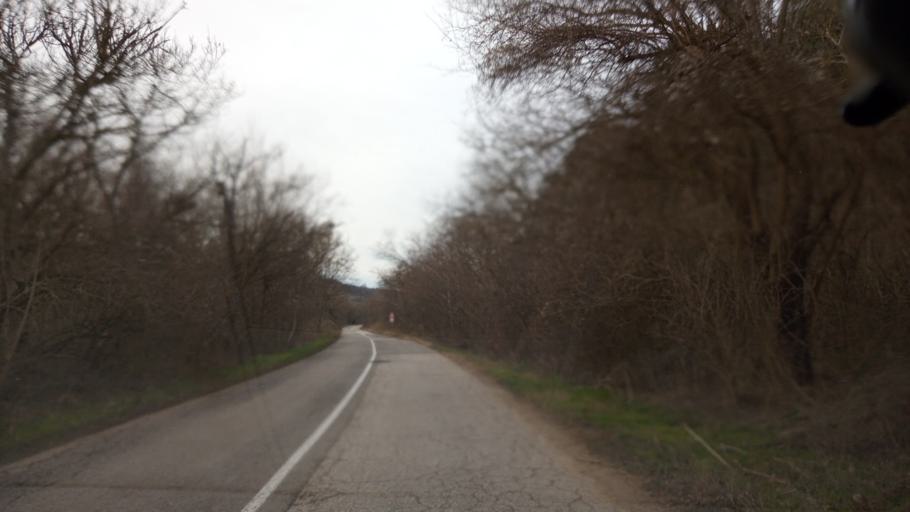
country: BG
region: Pleven
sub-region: Obshtina Belene
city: Belene
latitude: 43.6155
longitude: 25.0260
